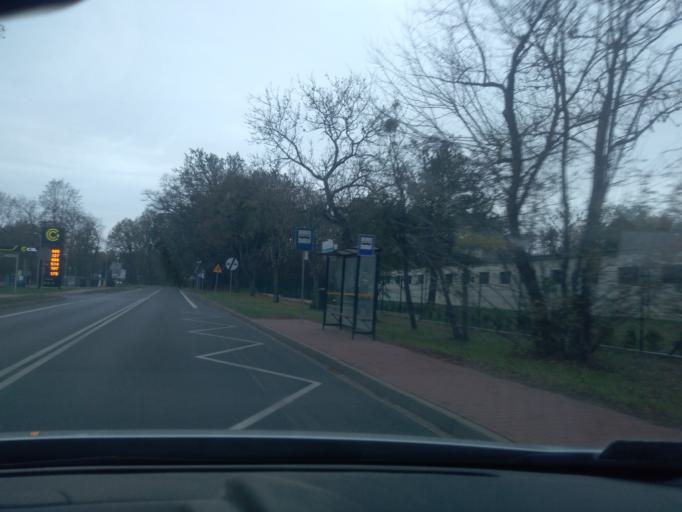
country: PL
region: Greater Poland Voivodeship
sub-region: Powiat poznanski
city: Murowana Goslina
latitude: 52.5360
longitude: 16.9436
